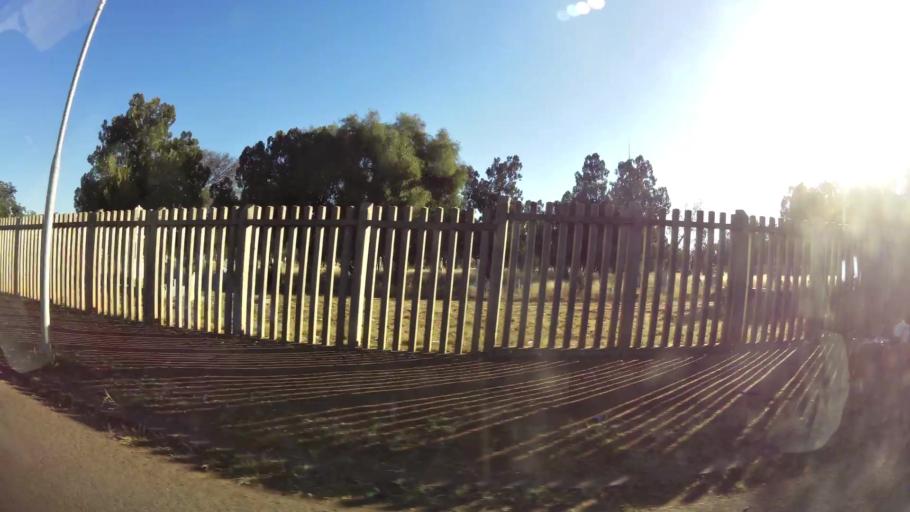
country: ZA
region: Northern Cape
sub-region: Frances Baard District Municipality
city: Kimberley
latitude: -28.7361
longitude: 24.7399
